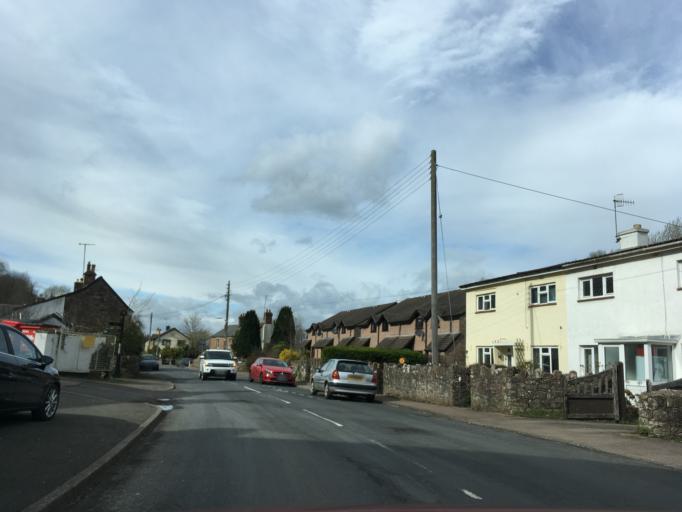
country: GB
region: England
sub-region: Gloucestershire
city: Coleford
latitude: 51.7698
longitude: -2.6221
